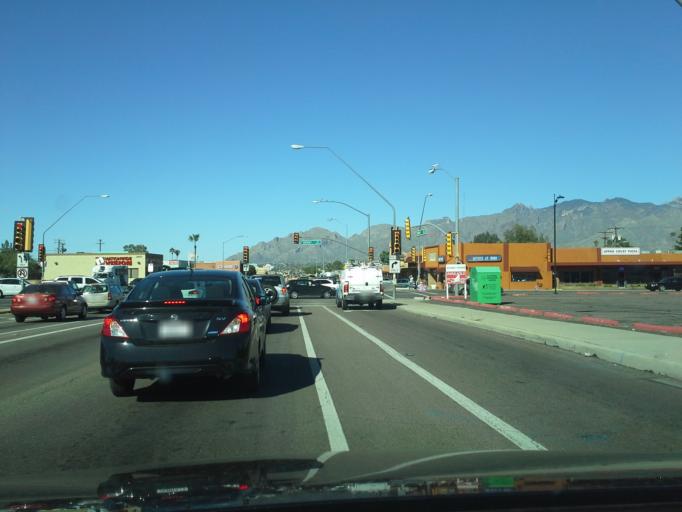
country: US
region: Arizona
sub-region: Pima County
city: Tucson
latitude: 32.2497
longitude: -110.9439
